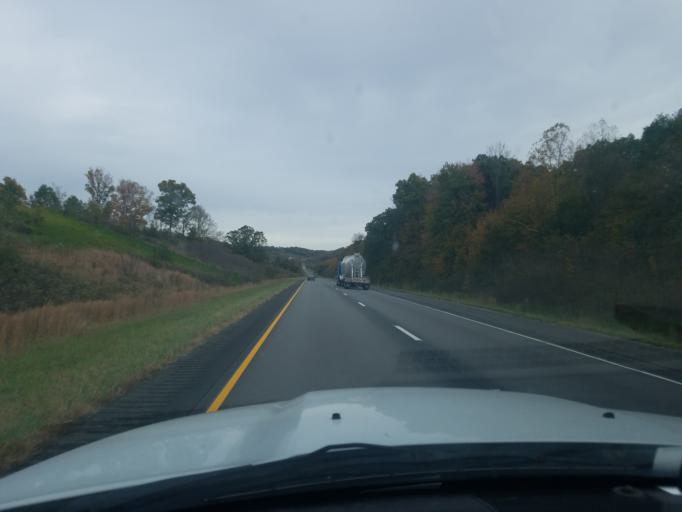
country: US
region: Indiana
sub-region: Dubois County
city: Ferdinand
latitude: 38.2038
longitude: -86.8181
